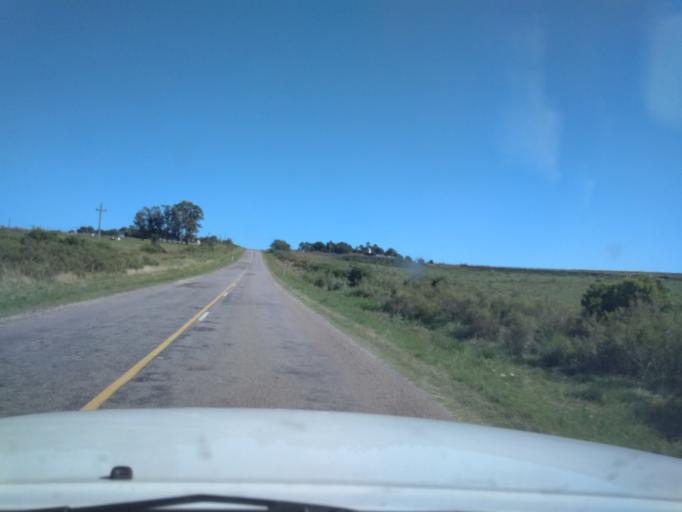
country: UY
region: Canelones
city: San Ramon
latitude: -34.1695
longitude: -55.9450
